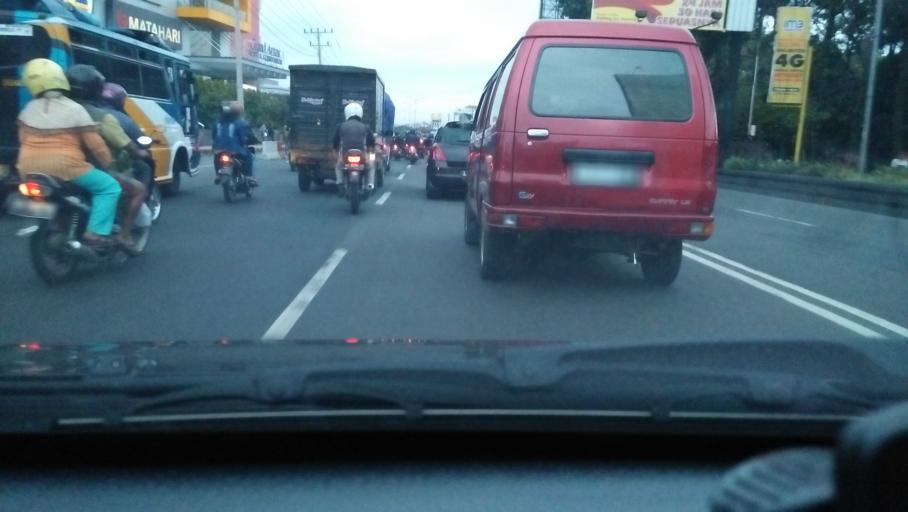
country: ID
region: Central Java
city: Mertoyudan
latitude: -7.5035
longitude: 110.2238
